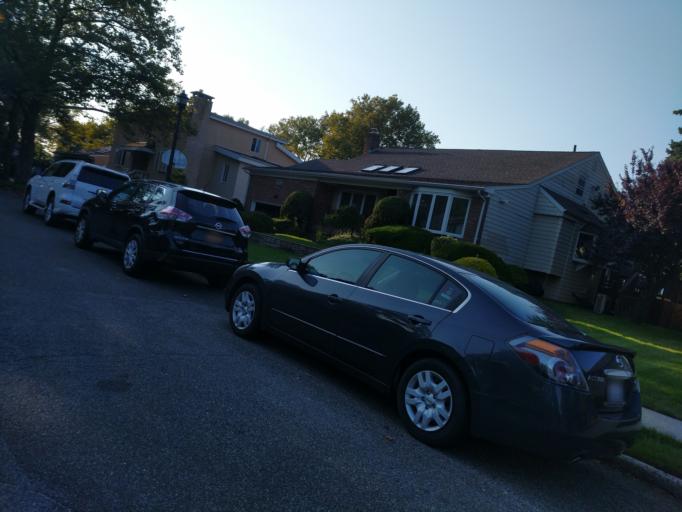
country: US
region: New York
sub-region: Nassau County
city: South Valley Stream
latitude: 40.6494
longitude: -73.7165
